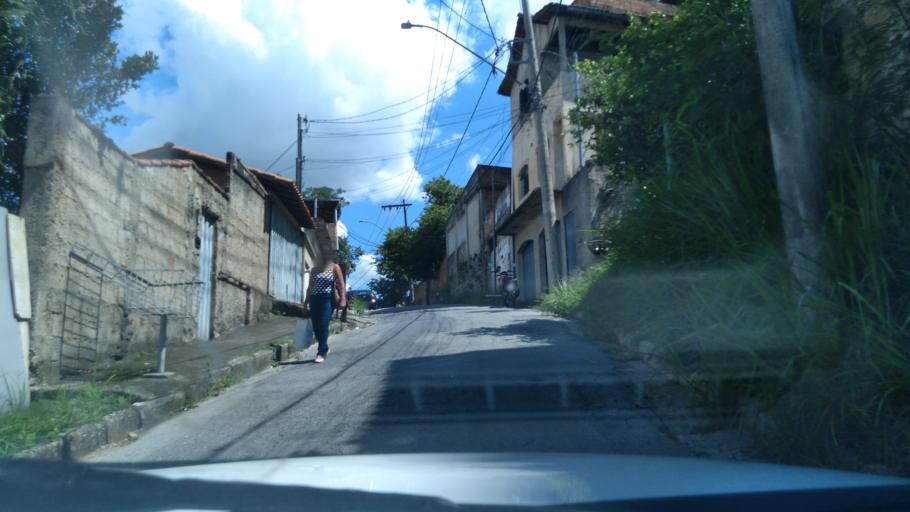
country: BR
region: Minas Gerais
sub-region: Belo Horizonte
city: Belo Horizonte
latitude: -19.8698
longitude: -43.9149
